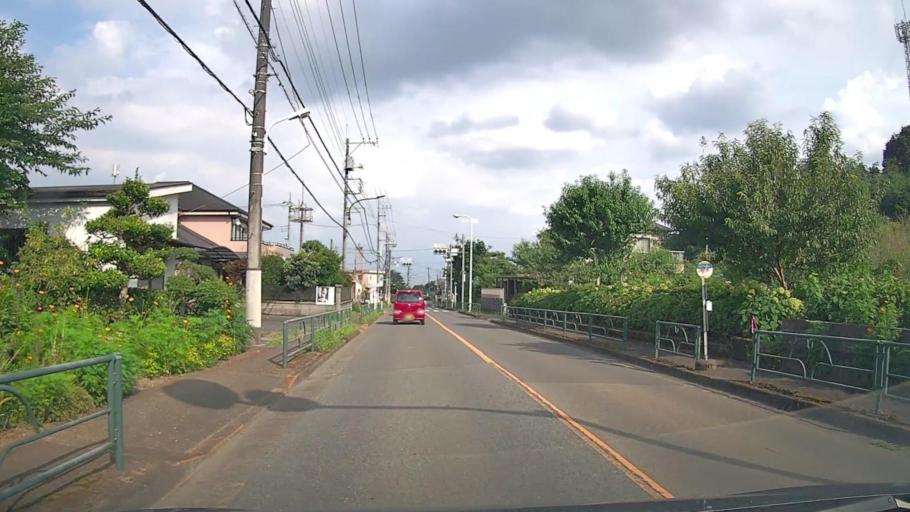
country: JP
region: Tokyo
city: Itsukaichi
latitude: 35.7043
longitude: 139.2534
